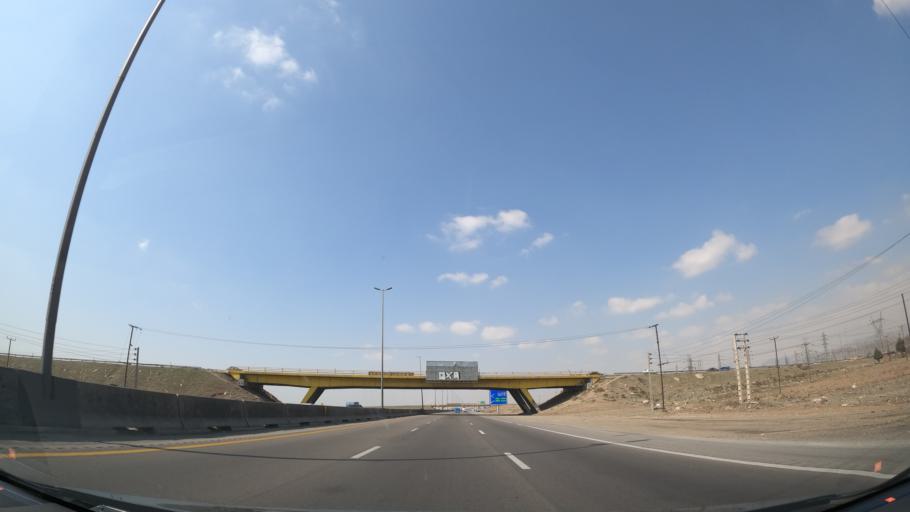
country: IR
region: Qazvin
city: Abyek
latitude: 36.0763
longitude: 50.4684
